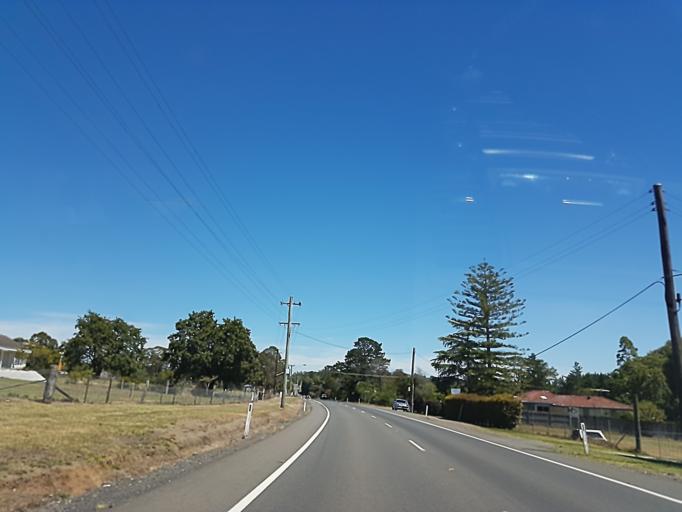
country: AU
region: New South Wales
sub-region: Hornsby Shire
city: Glenorie
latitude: -33.6060
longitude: 151.0148
